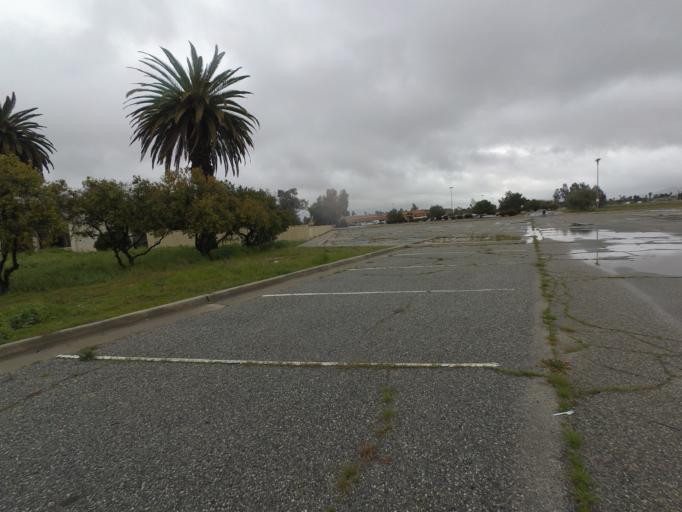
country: US
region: California
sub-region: Riverside County
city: March Air Force Base
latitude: 33.9004
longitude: -117.2480
